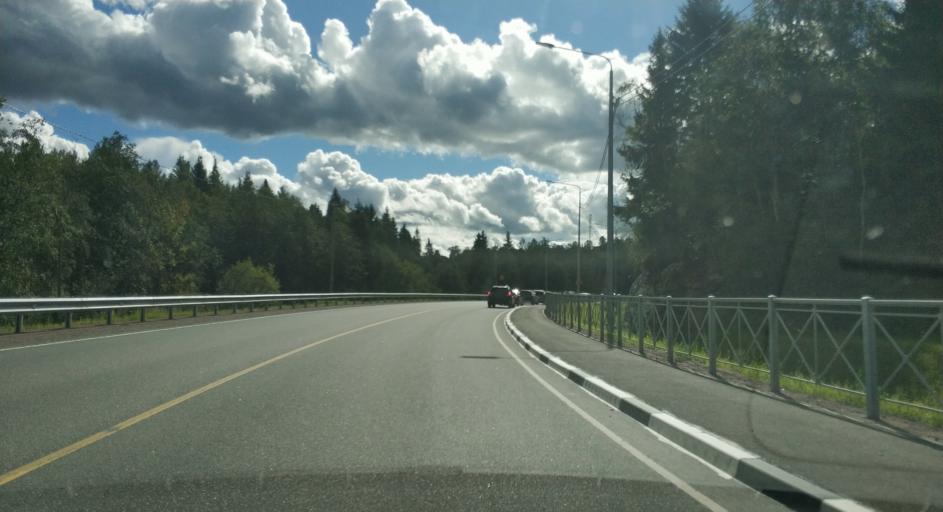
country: RU
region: Republic of Karelia
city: Ruskeala
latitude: 61.9394
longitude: 30.5918
